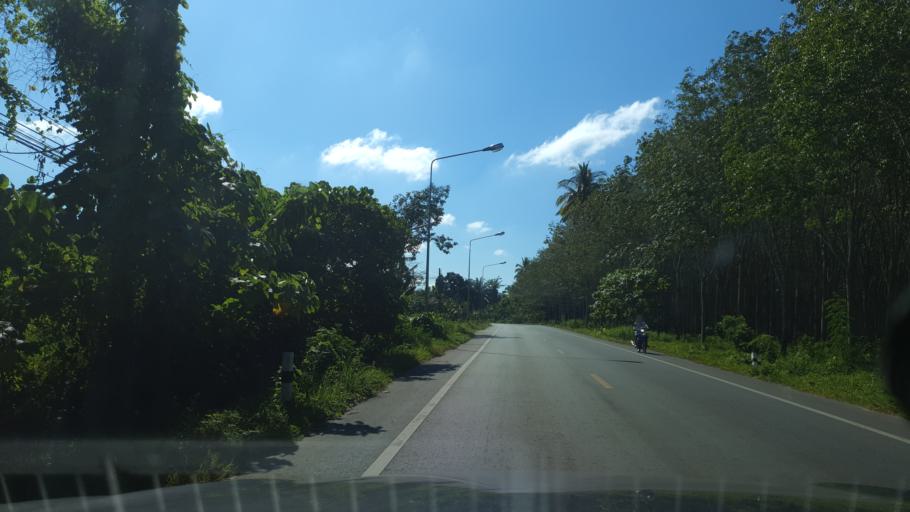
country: TH
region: Phangnga
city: Ban Ao Nang
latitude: 8.0733
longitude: 98.8068
